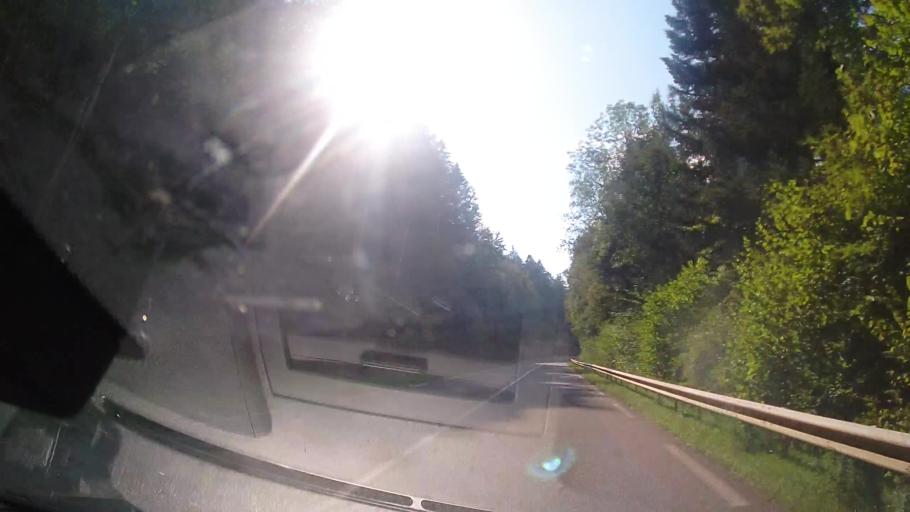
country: FR
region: Franche-Comte
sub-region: Departement du Jura
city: Clairvaux-les-Lacs
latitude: 46.5834
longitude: 5.8173
